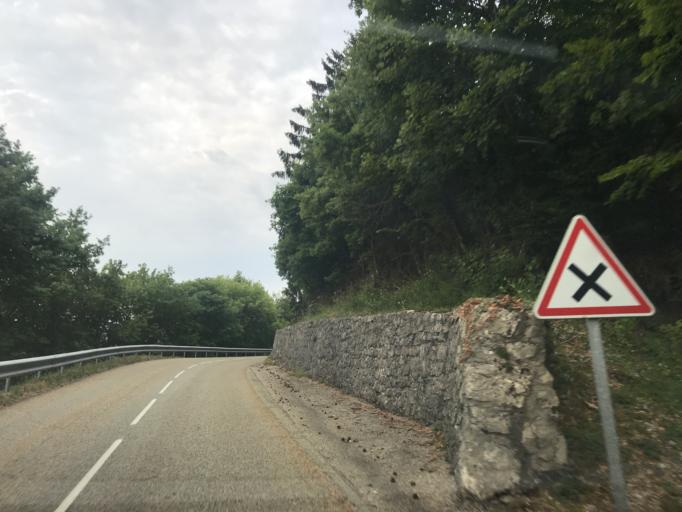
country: FR
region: Rhone-Alpes
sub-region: Departement de l'Isere
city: Saint-Vincent-de-Mercuze
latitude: 45.3938
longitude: 5.9566
